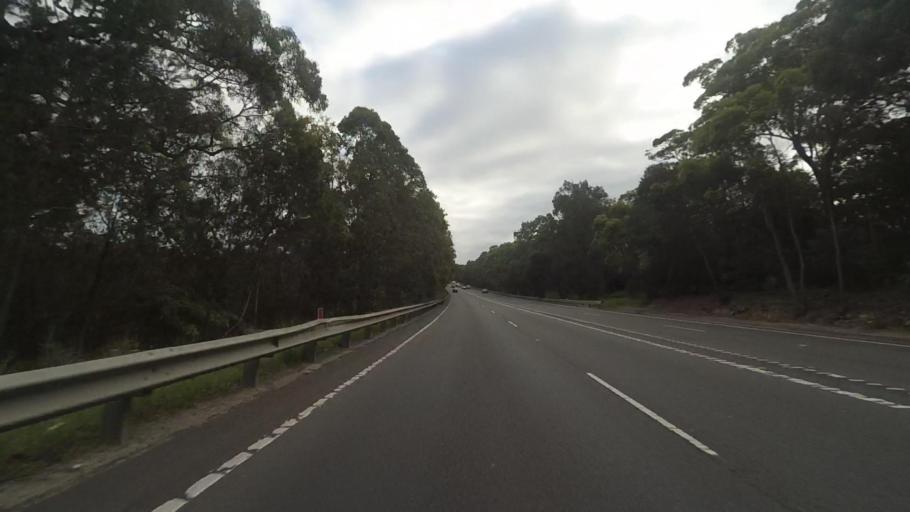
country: AU
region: New South Wales
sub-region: Sutherland Shire
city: Menai
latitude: -34.0068
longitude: 151.0132
